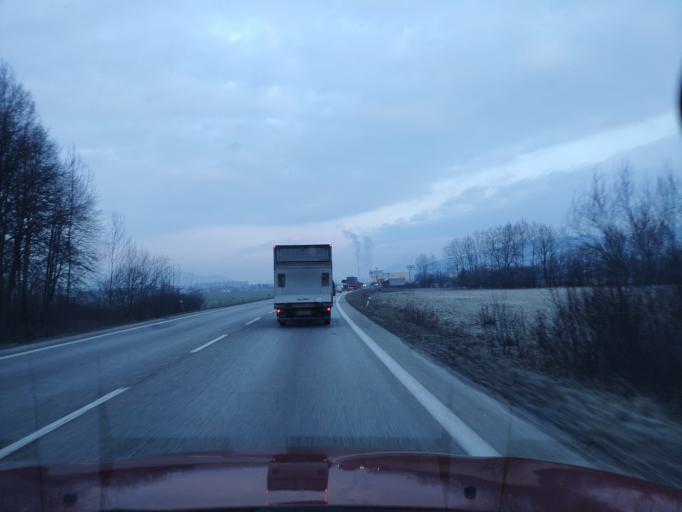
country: SK
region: Zilinsky
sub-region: Okres Zilina
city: Zilina
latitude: 49.2028
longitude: 18.7914
